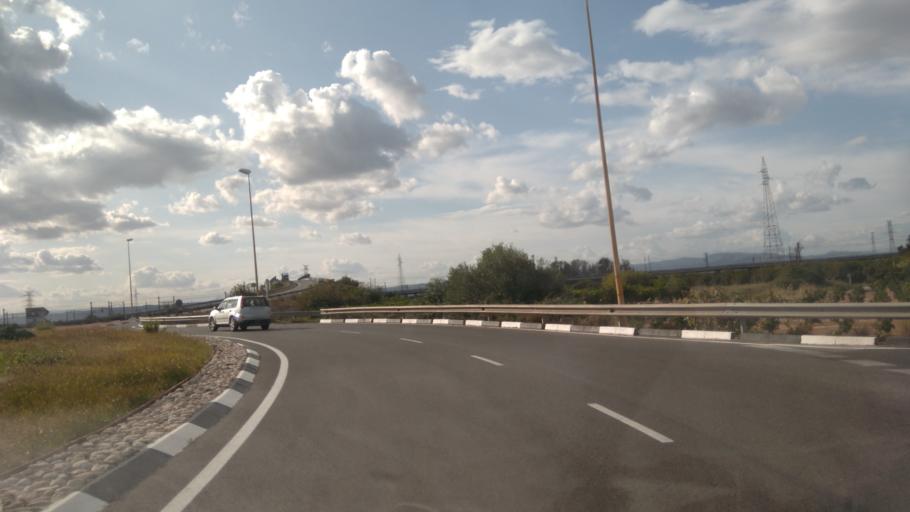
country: ES
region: Valencia
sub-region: Provincia de Valencia
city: Alzira
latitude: 39.1639
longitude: -0.4453
